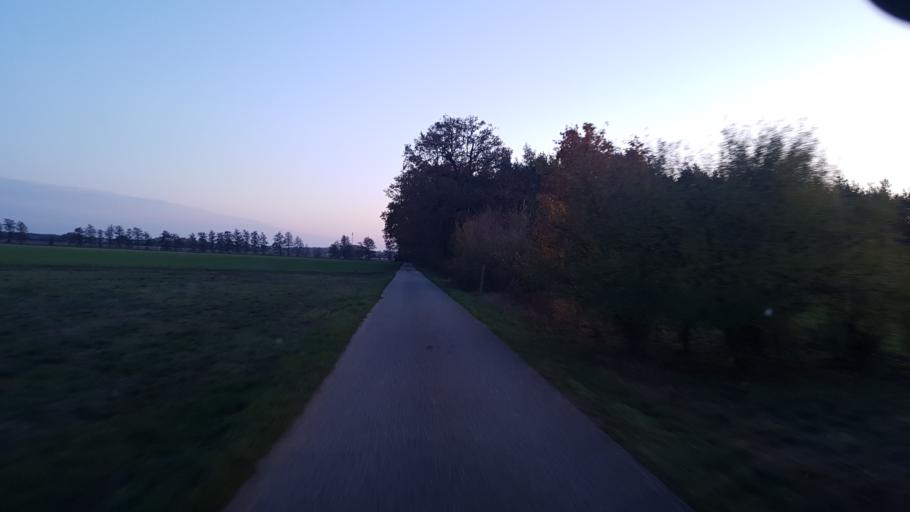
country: DE
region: Brandenburg
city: Schilda
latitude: 51.6272
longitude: 13.3301
